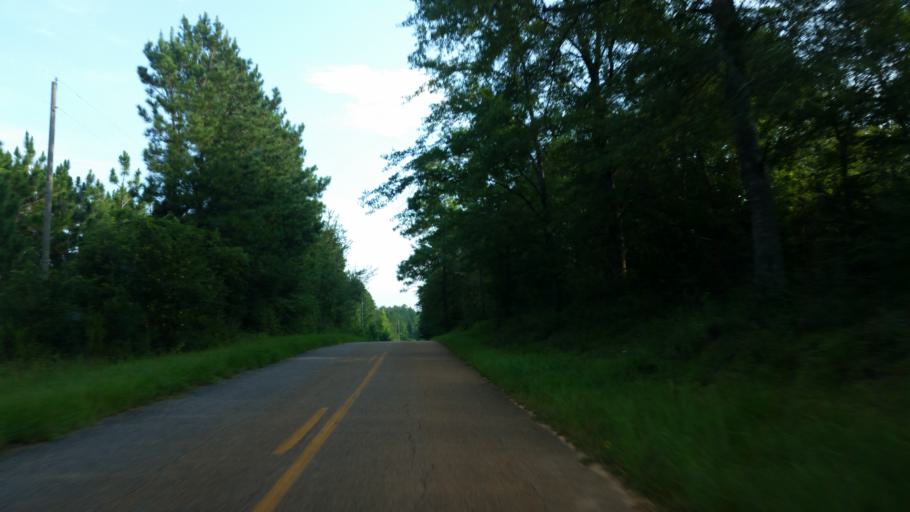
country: US
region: Alabama
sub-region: Escambia County
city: Atmore
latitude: 30.9696
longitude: -87.5714
